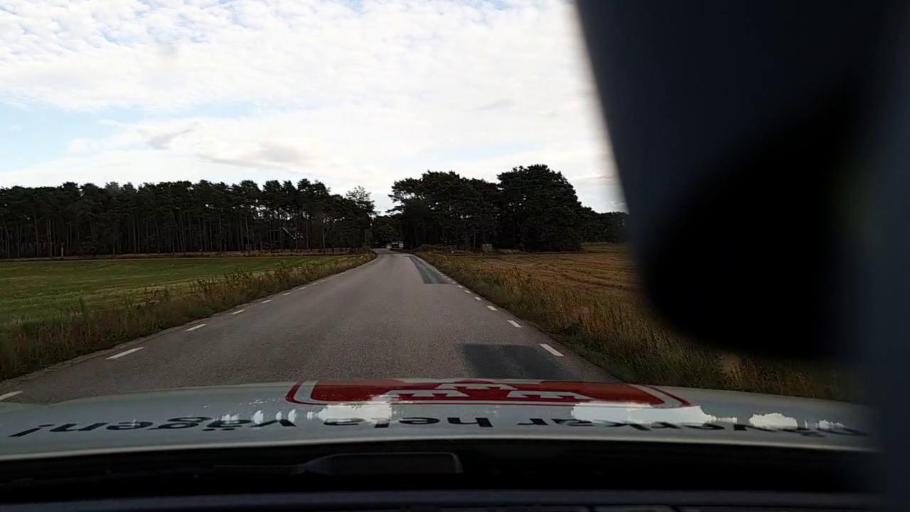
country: SE
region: Blekinge
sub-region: Solvesborgs Kommun
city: Soelvesborg
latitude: 56.0256
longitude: 14.7151
